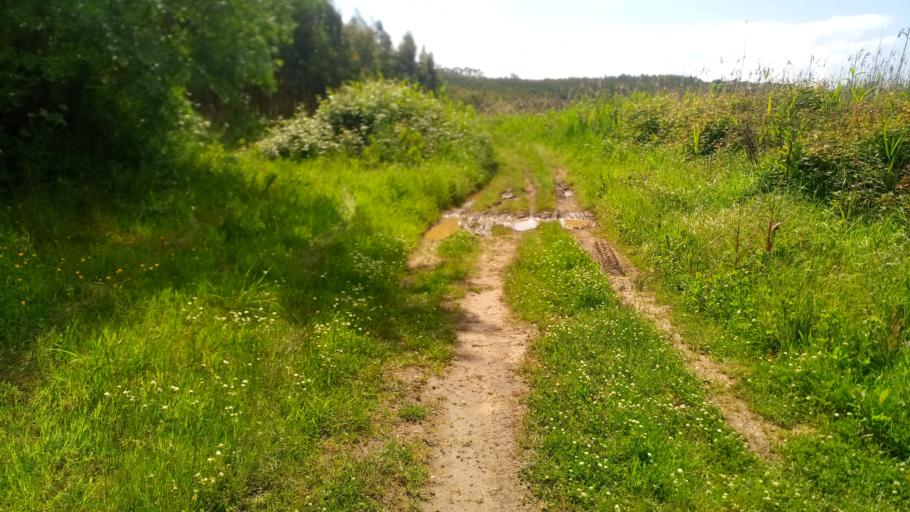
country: PT
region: Leiria
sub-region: Caldas da Rainha
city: Caldas da Rainha
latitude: 39.4000
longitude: -9.1830
